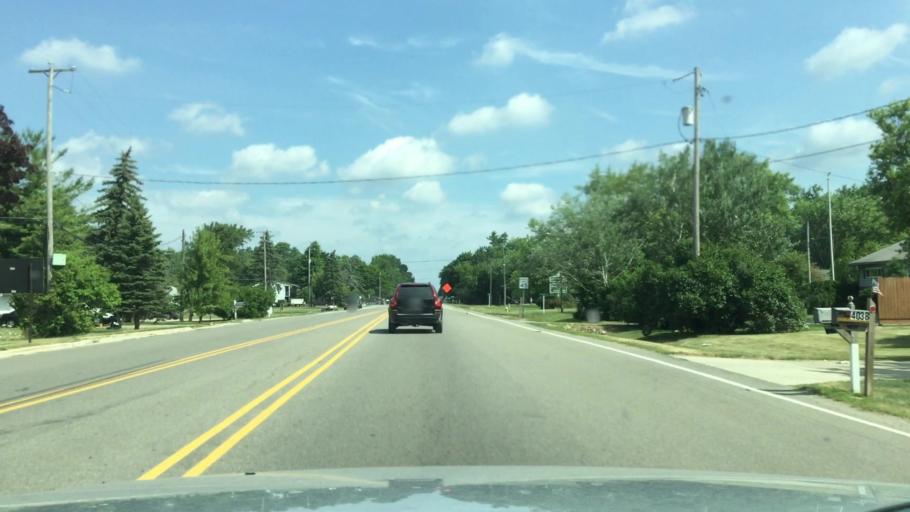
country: US
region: Michigan
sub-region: Genesee County
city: Flushing
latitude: 43.0613
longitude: -83.8132
